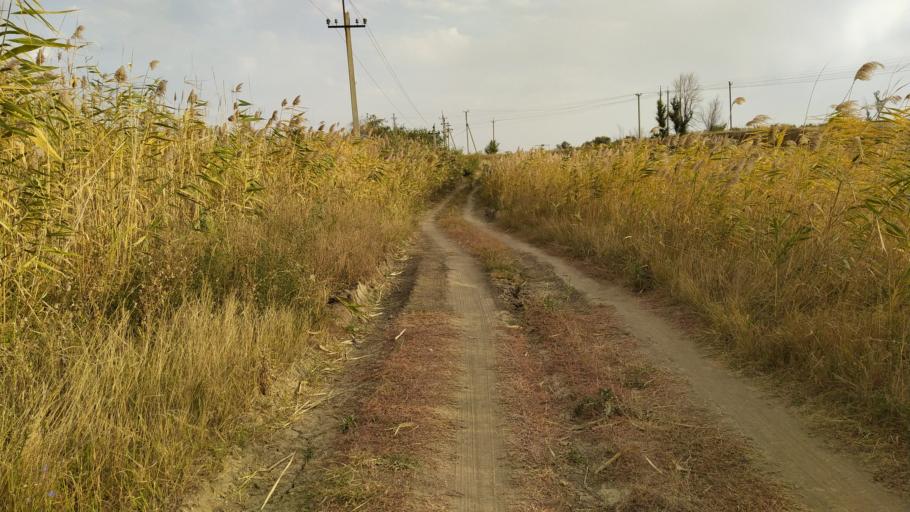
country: RU
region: Rostov
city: Kuleshovka
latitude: 47.1098
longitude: 39.6130
